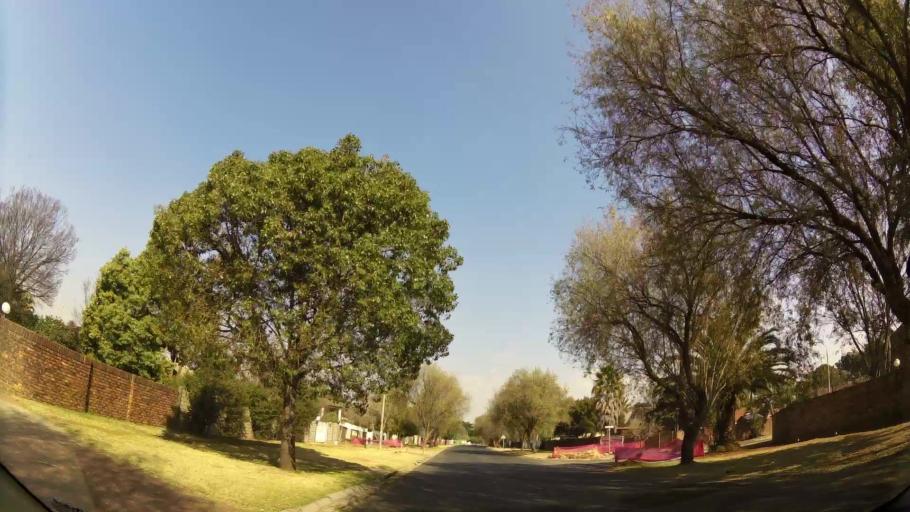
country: ZA
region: Gauteng
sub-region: Ekurhuleni Metropolitan Municipality
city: Benoni
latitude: -26.1505
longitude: 28.2838
